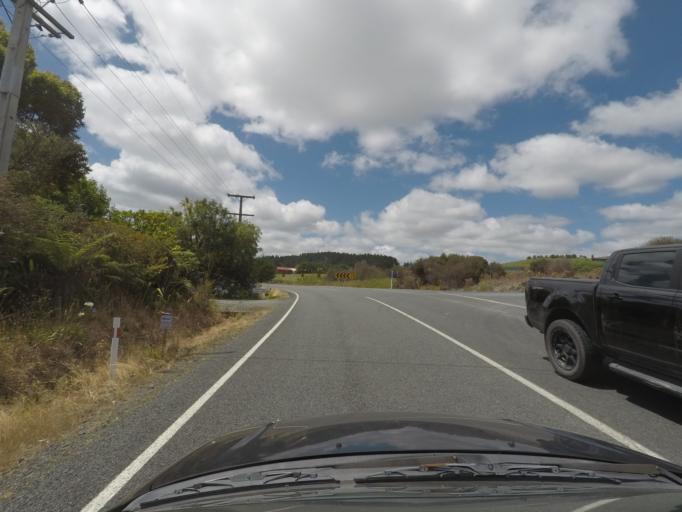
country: NZ
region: Northland
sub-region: Whangarei
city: Ruakaka
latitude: -36.0138
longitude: 174.4836
